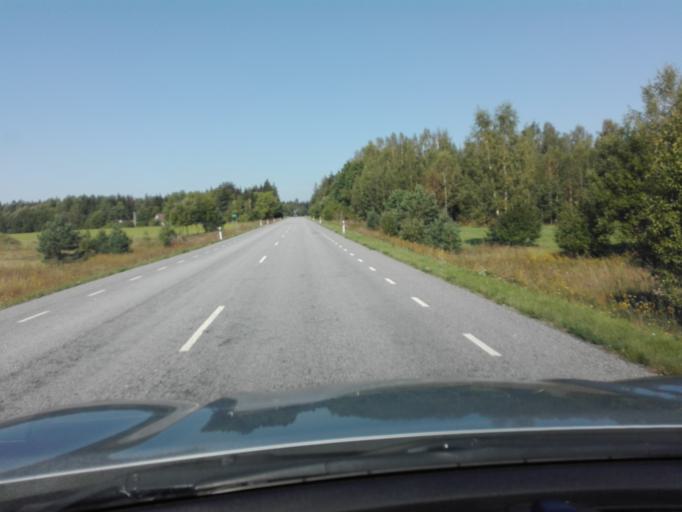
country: EE
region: Raplamaa
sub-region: Rapla vald
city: Rapla
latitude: 59.0005
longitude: 24.7689
